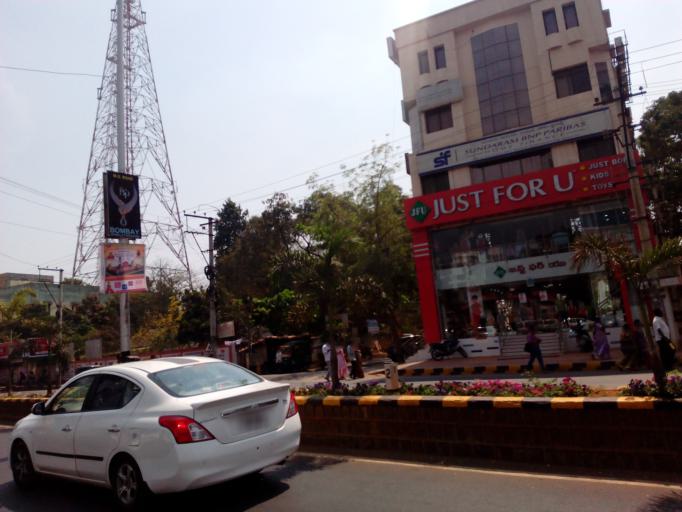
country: IN
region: Andhra Pradesh
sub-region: Krishna
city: Yanamalakuduru
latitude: 16.4995
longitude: 80.6497
